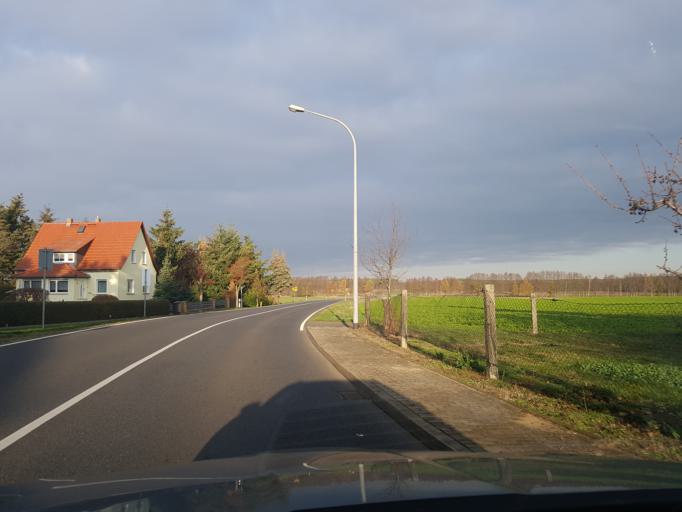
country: DE
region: Brandenburg
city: Kasel-Golzig
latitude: 51.9003
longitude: 13.6772
